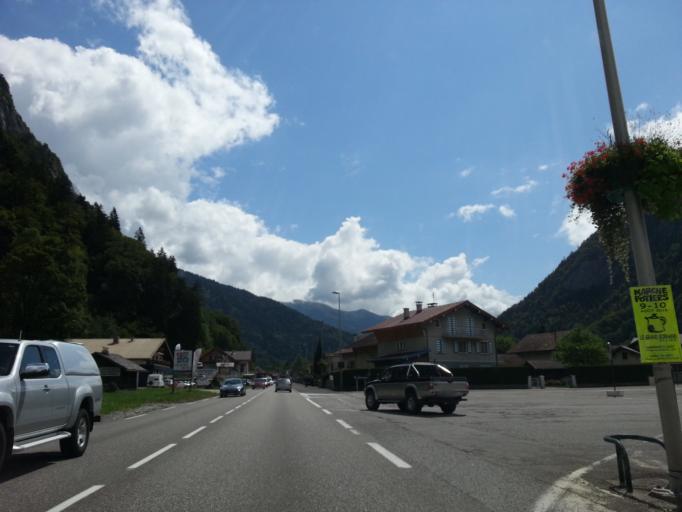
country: FR
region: Rhone-Alpes
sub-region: Departement de la Haute-Savoie
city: Thones
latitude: 45.8895
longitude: 6.3119
